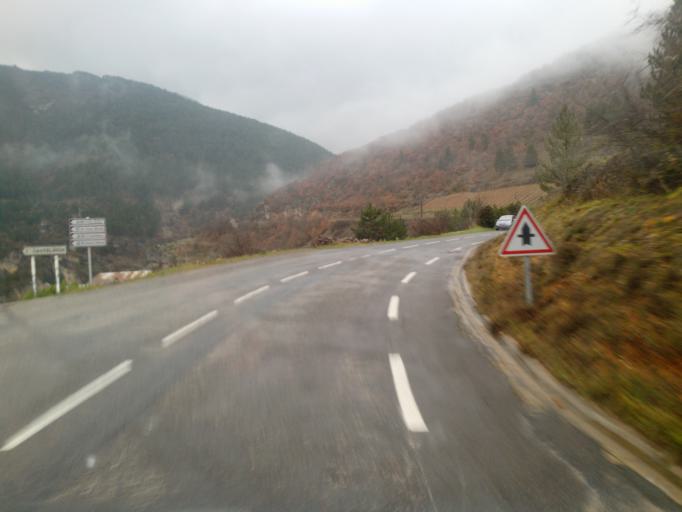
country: FR
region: Languedoc-Roussillon
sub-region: Departement de la Lozere
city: Florac
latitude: 44.3394
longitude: 3.4736
